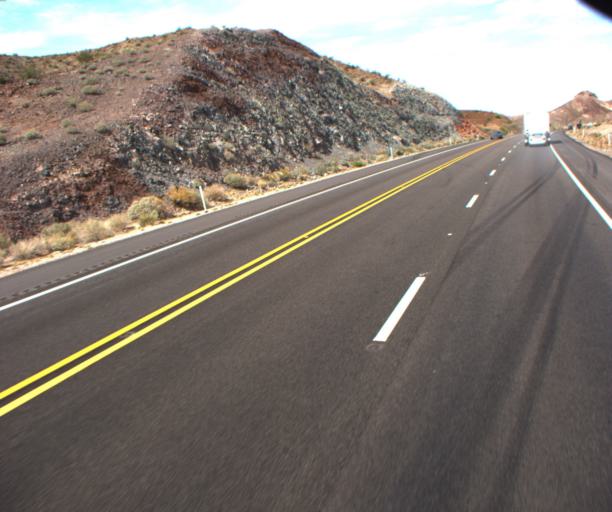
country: US
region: Arizona
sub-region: Mohave County
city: Desert Hills
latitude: 34.6011
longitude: -114.3661
